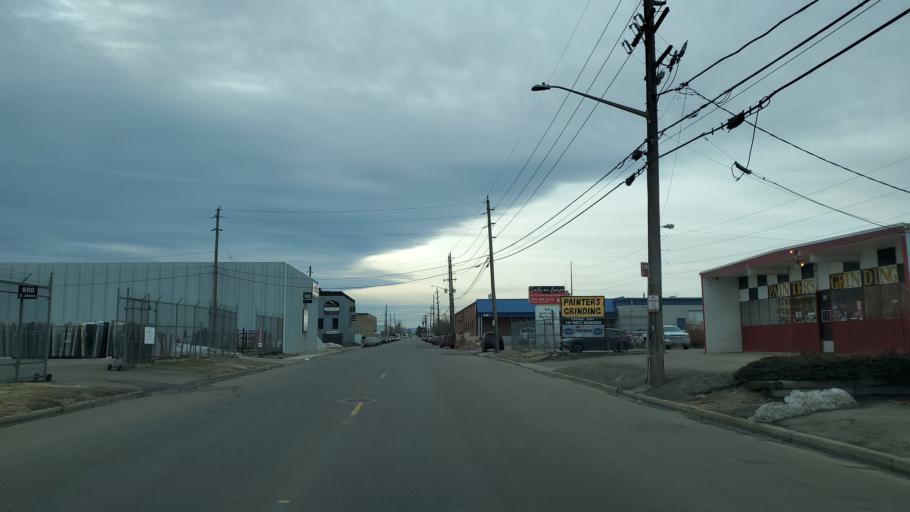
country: US
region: Colorado
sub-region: Denver County
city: Denver
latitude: 39.7018
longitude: -104.9992
